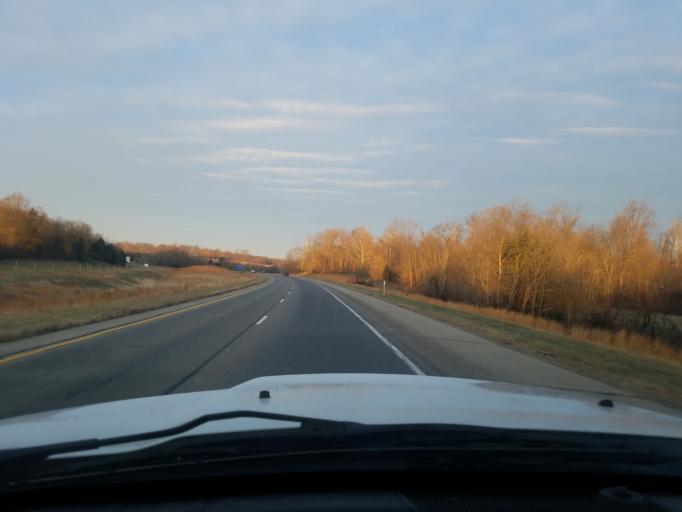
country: US
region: Indiana
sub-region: Floyd County
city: Georgetown
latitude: 38.2843
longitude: -85.9330
